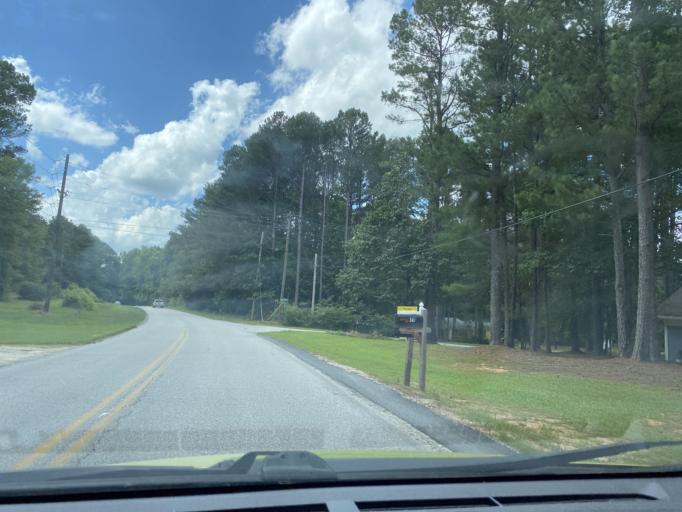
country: US
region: Georgia
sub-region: Fayette County
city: Peachtree City
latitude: 33.4166
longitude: -84.6953
